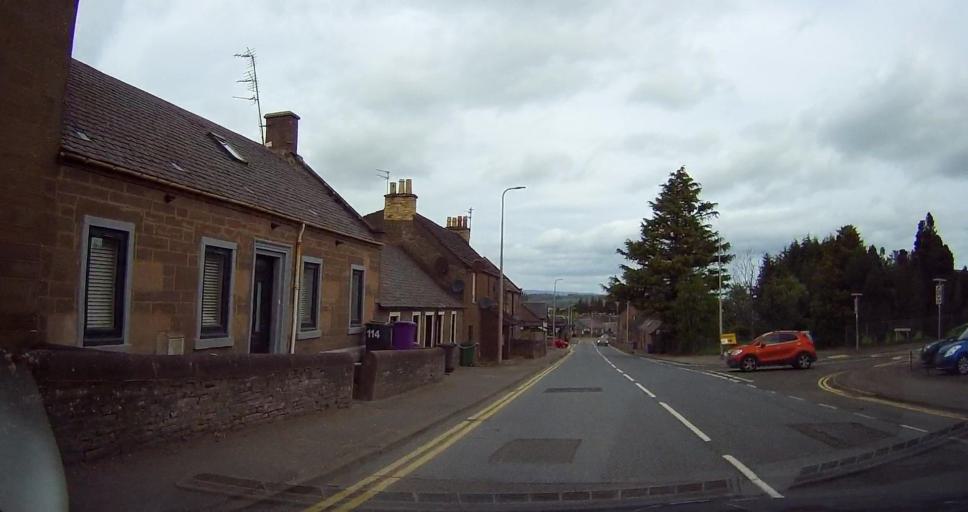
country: GB
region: Scotland
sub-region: Angus
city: Forfar
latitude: 56.6363
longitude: -2.8948
